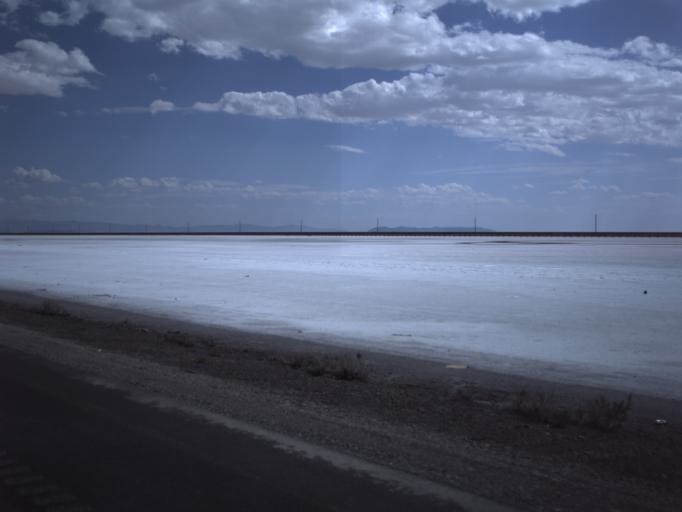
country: US
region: Utah
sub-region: Tooele County
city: Wendover
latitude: 40.7344
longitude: -113.6572
